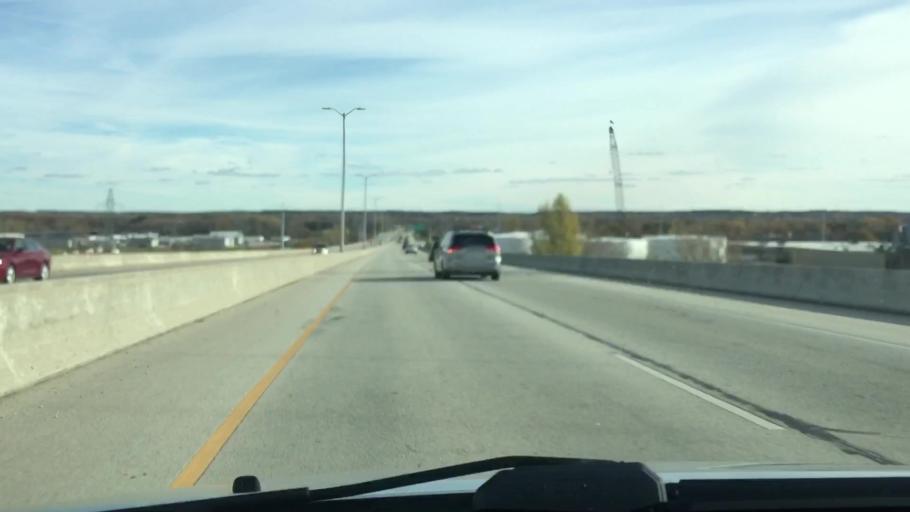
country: US
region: Wisconsin
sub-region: Brown County
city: Green Bay
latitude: 44.5304
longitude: -87.9987
